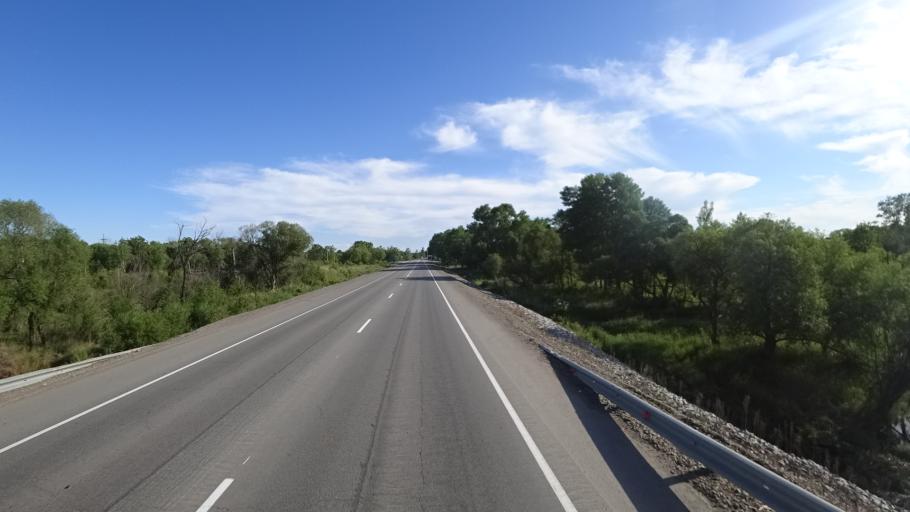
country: RU
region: Khabarovsk Krai
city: Khor
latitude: 47.8592
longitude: 134.9627
